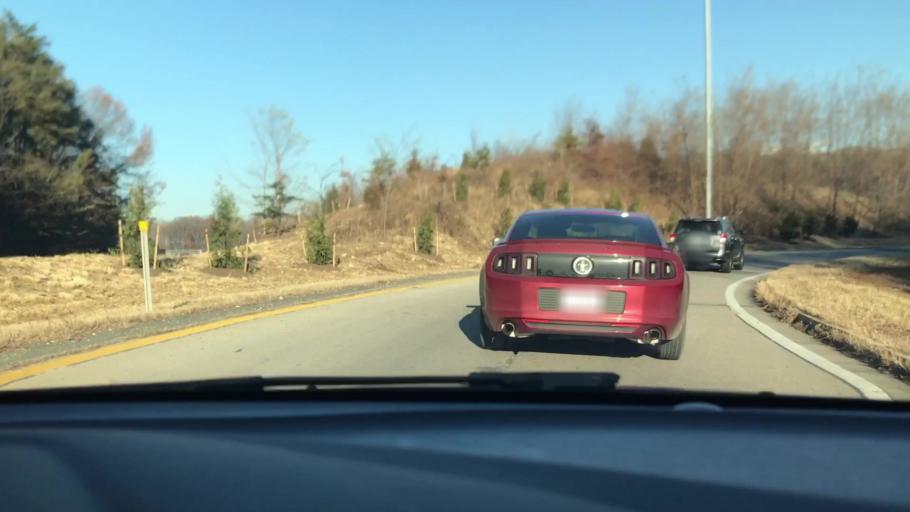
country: US
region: Virginia
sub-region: Fairfax County
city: Merrifield
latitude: 38.8671
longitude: -77.2219
